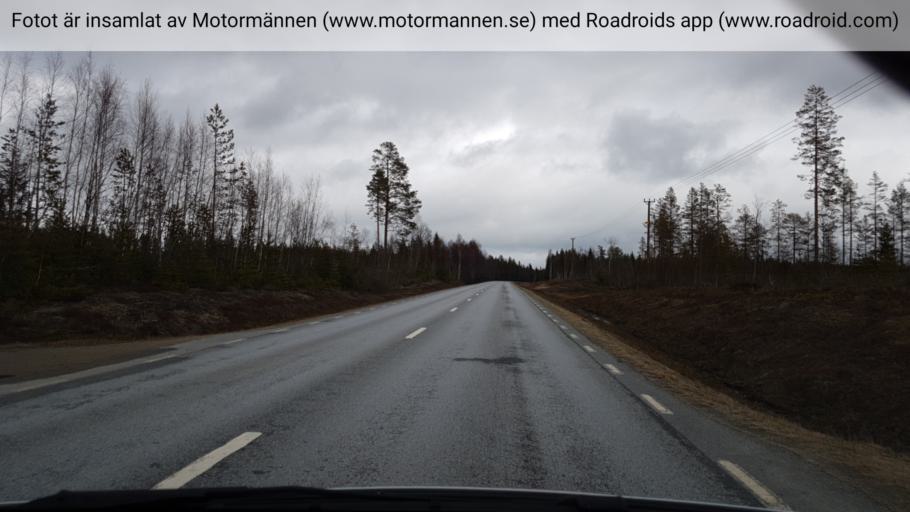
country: SE
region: Vaesterbotten
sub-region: Vannas Kommun
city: Vaennaes
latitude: 63.9308
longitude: 19.4880
